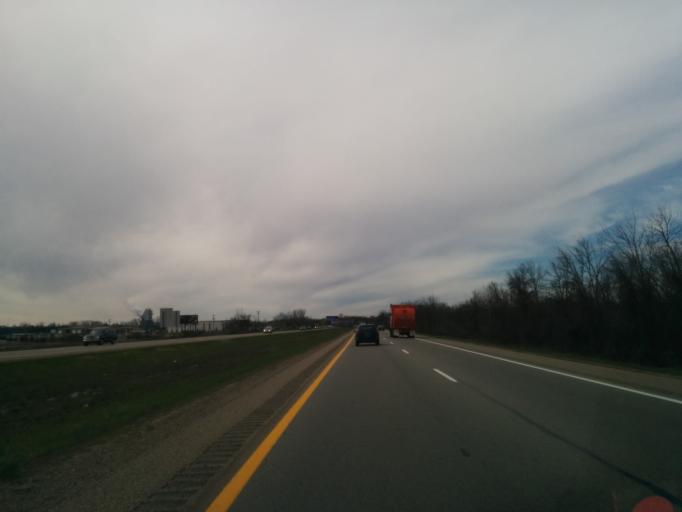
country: US
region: Michigan
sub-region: Kent County
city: Grandville
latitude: 42.9247
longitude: -85.7505
